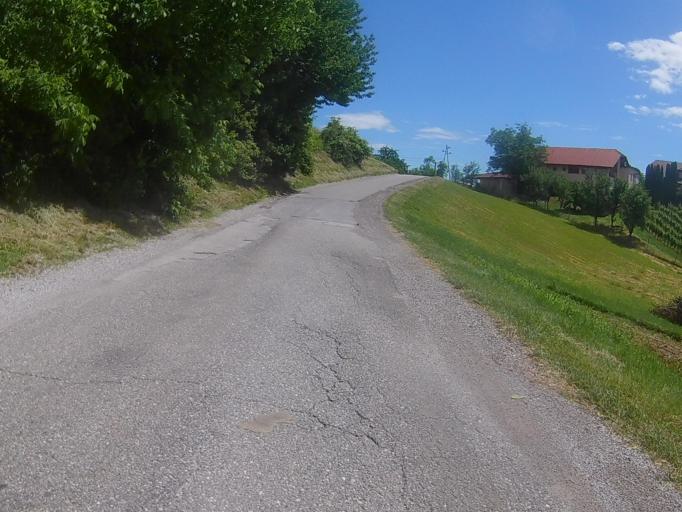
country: SI
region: Duplek
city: Zgornji Duplek
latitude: 46.5545
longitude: 15.7215
